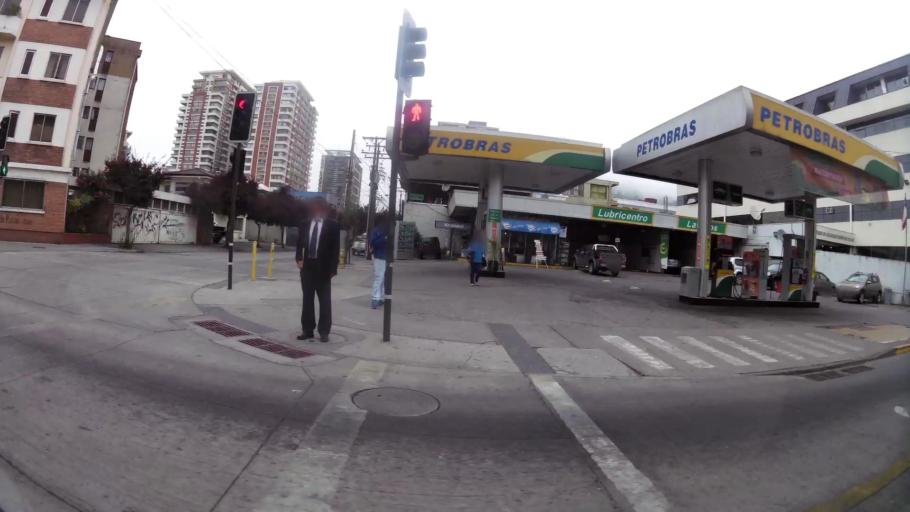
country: CL
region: Biobio
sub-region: Provincia de Concepcion
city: Concepcion
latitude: -36.8262
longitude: -73.0437
